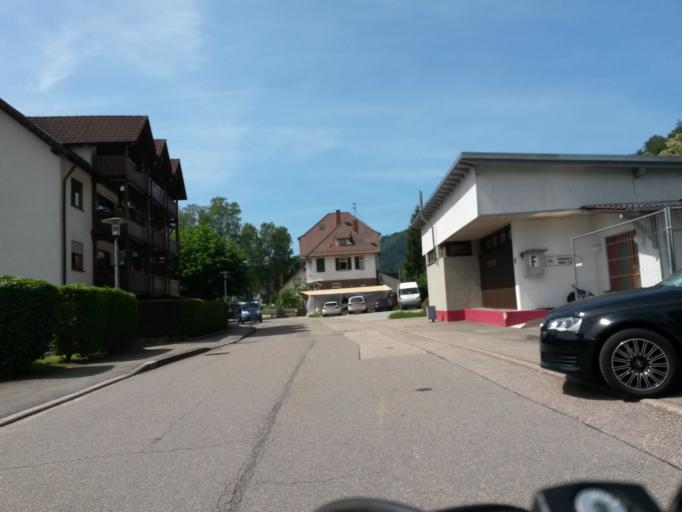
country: DE
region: Baden-Wuerttemberg
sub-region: Karlsruhe Region
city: Hofen an der Enz
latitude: 48.7765
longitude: 8.5715
